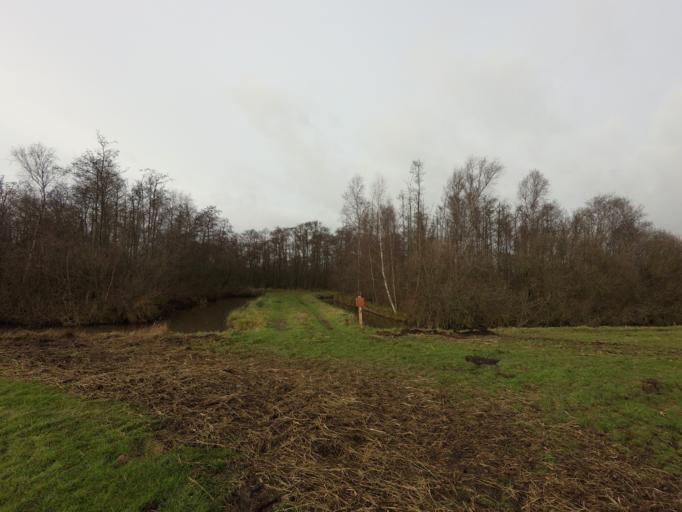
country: NL
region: North Holland
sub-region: Gemeente Wijdemeren
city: Nieuw-Loosdrecht
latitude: 52.1633
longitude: 5.1192
